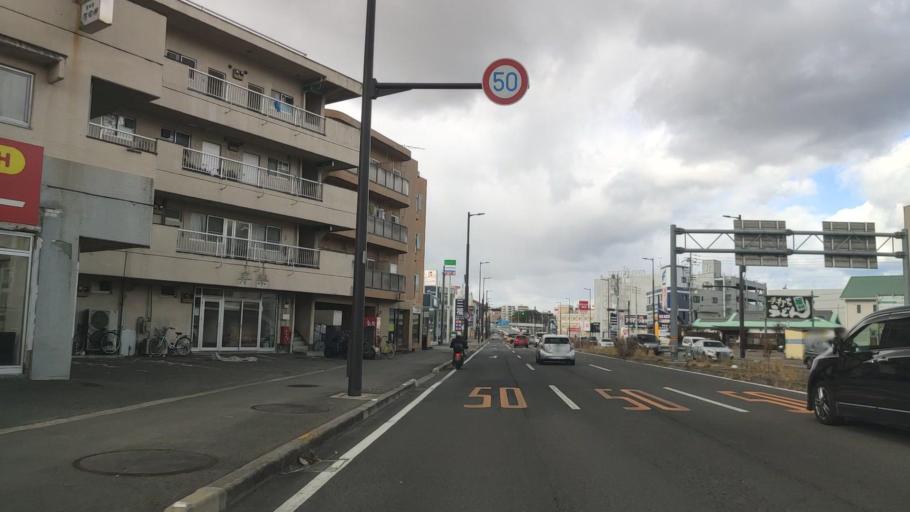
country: JP
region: Ehime
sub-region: Shikoku-chuo Shi
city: Matsuyama
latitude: 33.8308
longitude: 132.7799
